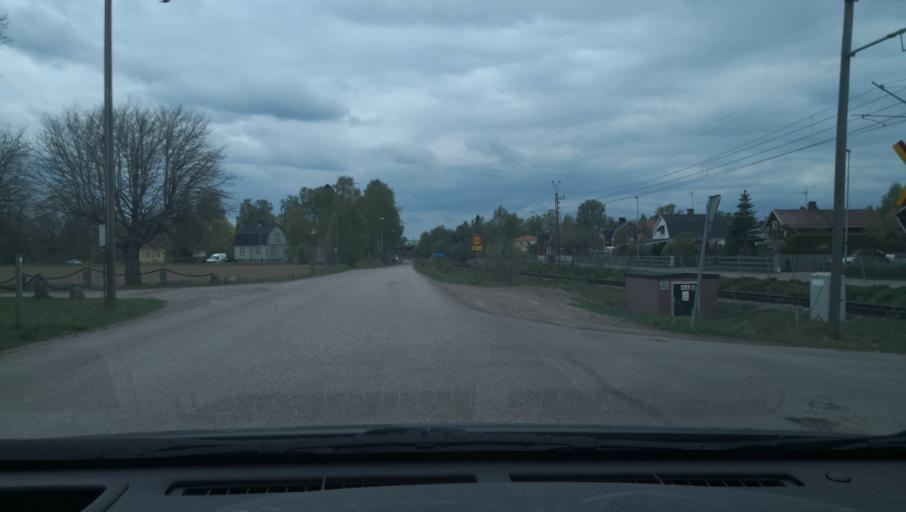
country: SE
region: Dalarna
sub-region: Avesta Kommun
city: Avesta
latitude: 60.1396
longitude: 16.2198
